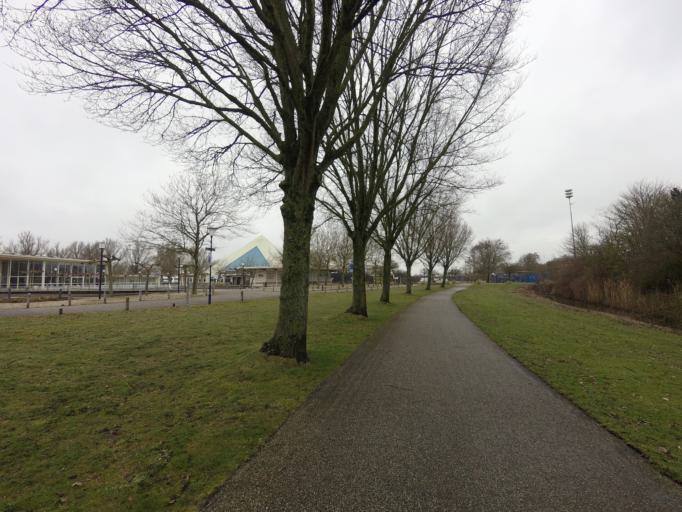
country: NL
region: Friesland
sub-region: Sudwest Fryslan
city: Makkum
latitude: 53.0531
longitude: 5.3848
